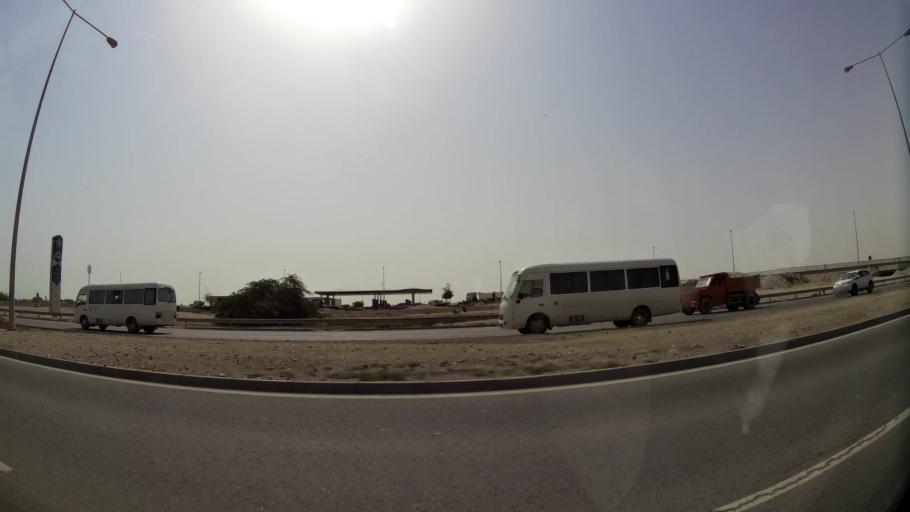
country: QA
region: Baladiyat ad Dawhah
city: Doha
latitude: 25.2302
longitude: 51.5139
